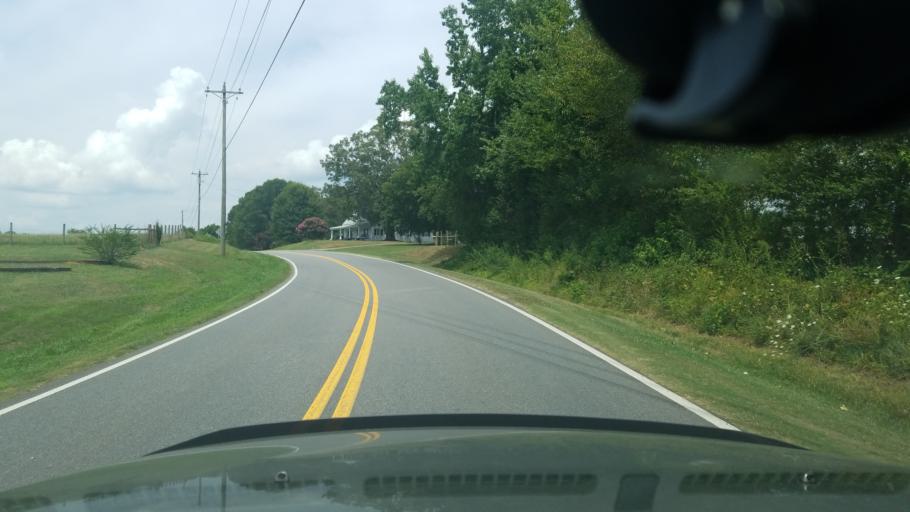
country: US
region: Georgia
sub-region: Forsyth County
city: Cumming
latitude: 34.2409
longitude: -84.2530
